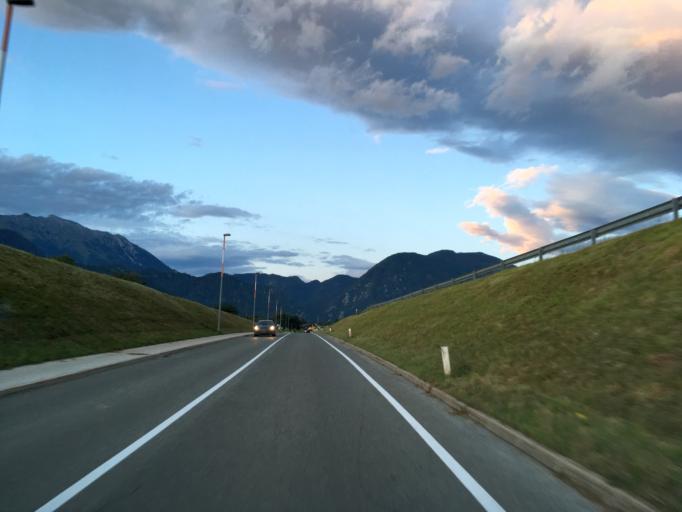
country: SI
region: Radovljica
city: Lesce
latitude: 46.3626
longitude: 14.1673
